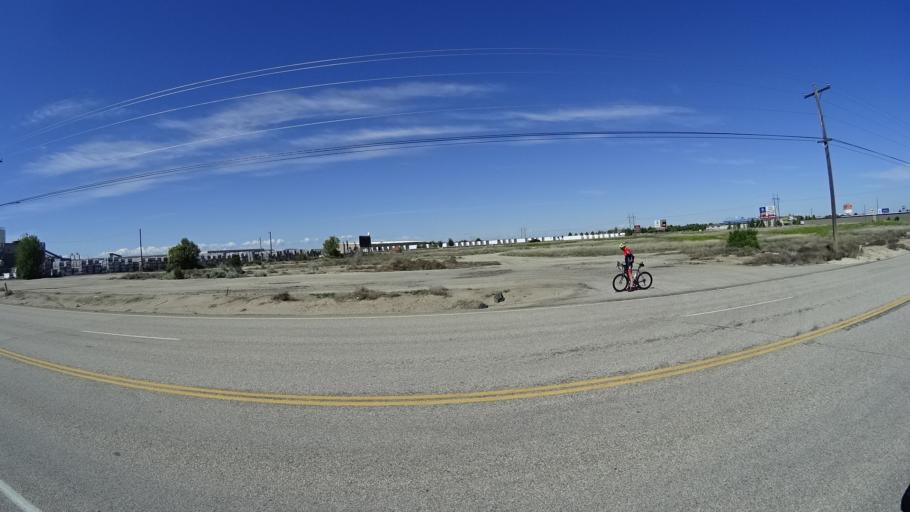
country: US
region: Idaho
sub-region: Ada County
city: Boise
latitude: 43.5358
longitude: -116.1533
